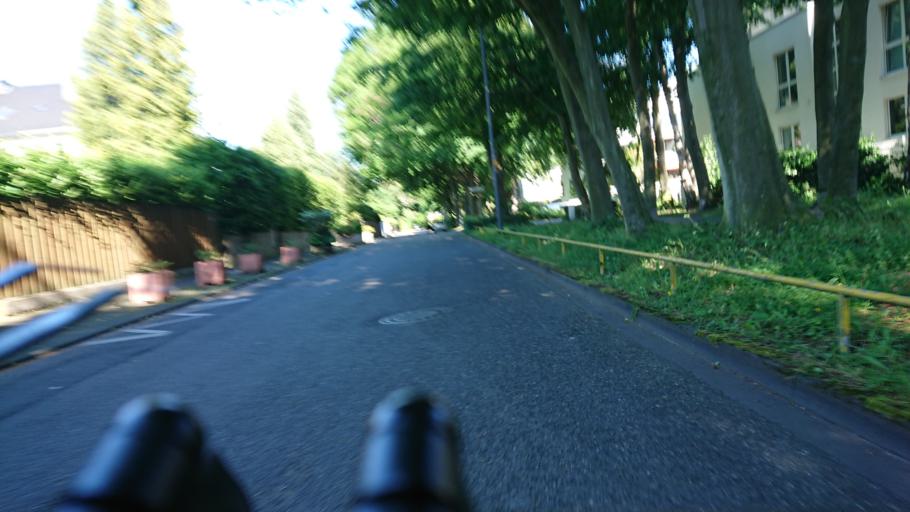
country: DE
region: North Rhine-Westphalia
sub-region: Regierungsbezirk Koln
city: Mengenich
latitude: 50.9354
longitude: 6.8578
